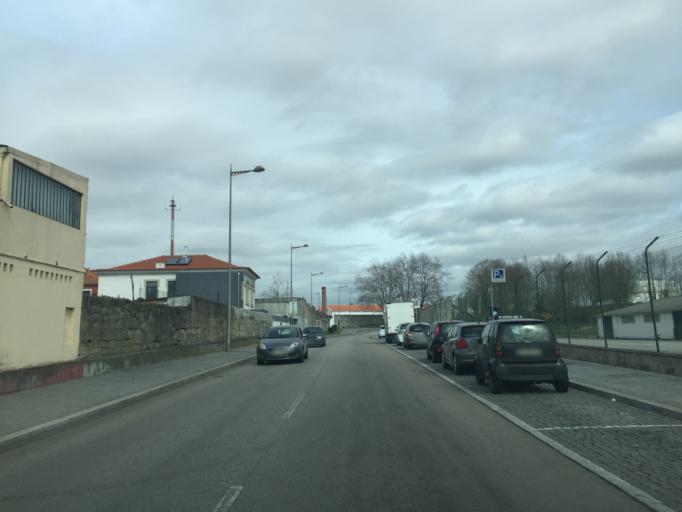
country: PT
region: Porto
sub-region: Vila Nova de Gaia
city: Vila Nova de Gaia
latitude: 41.1364
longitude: -8.6045
